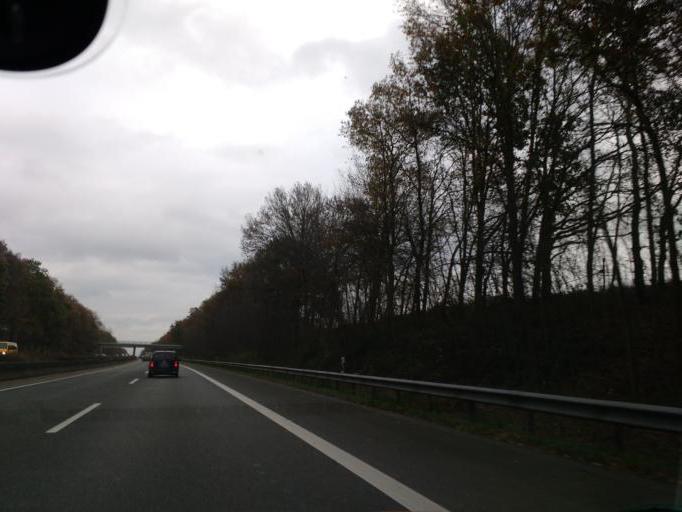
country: DE
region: Lower Saxony
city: Ahsen-Oetzen
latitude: 53.0140
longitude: 9.0895
